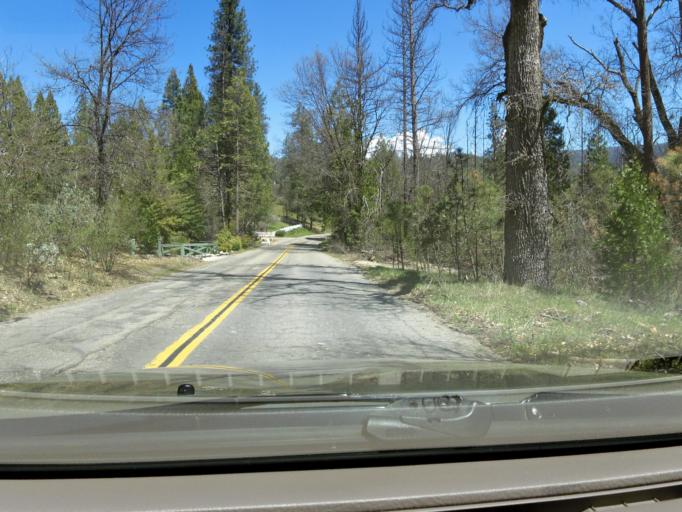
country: US
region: California
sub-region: Madera County
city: Oakhurst
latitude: 37.3308
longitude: -119.5827
